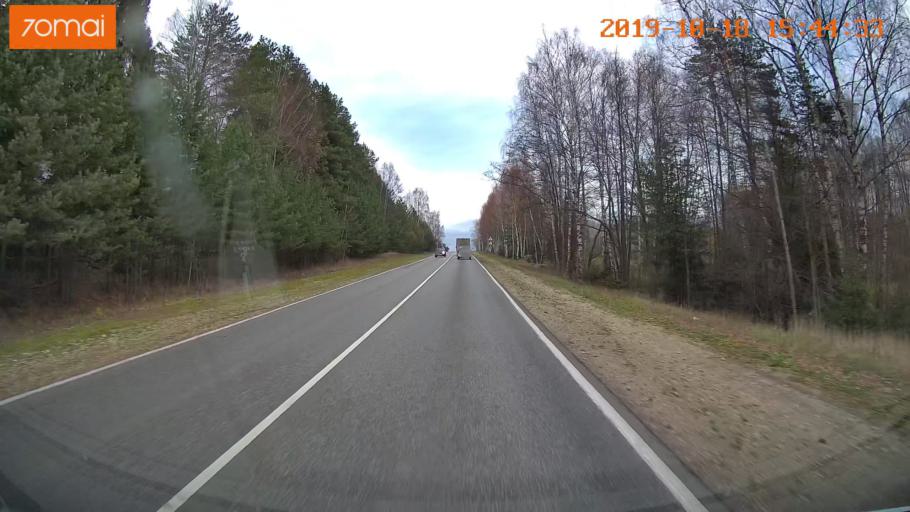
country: RU
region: Vladimir
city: Golovino
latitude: 55.9828
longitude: 40.5517
